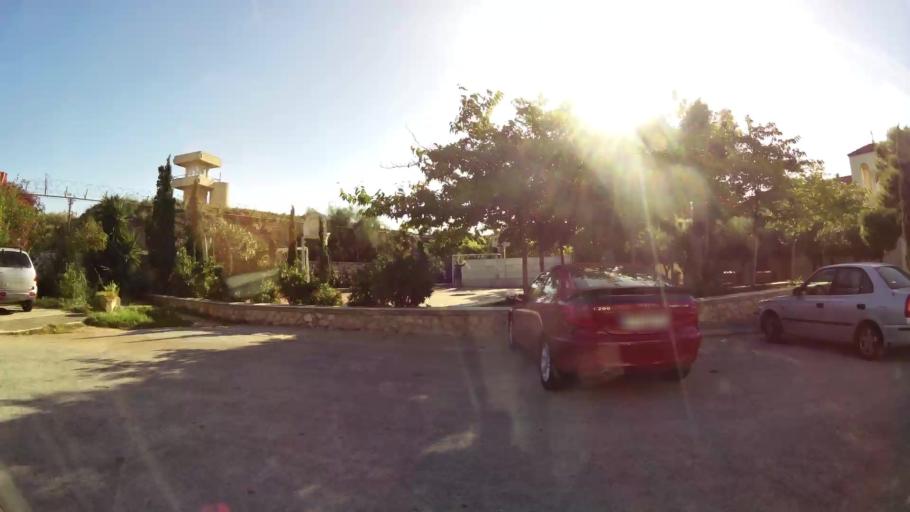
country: GR
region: Attica
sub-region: Nomarchia Athinas
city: Elliniko
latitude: 37.8748
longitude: 23.7366
